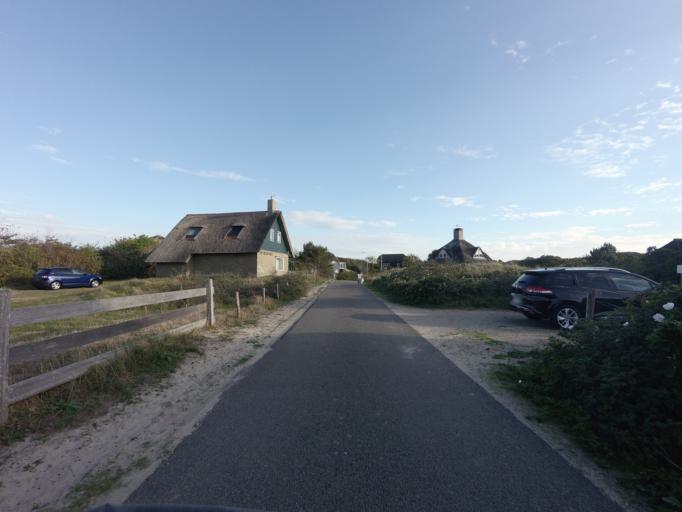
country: NL
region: Friesland
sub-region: Gemeente Ameland
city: Nes
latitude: 53.4581
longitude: 5.8017
